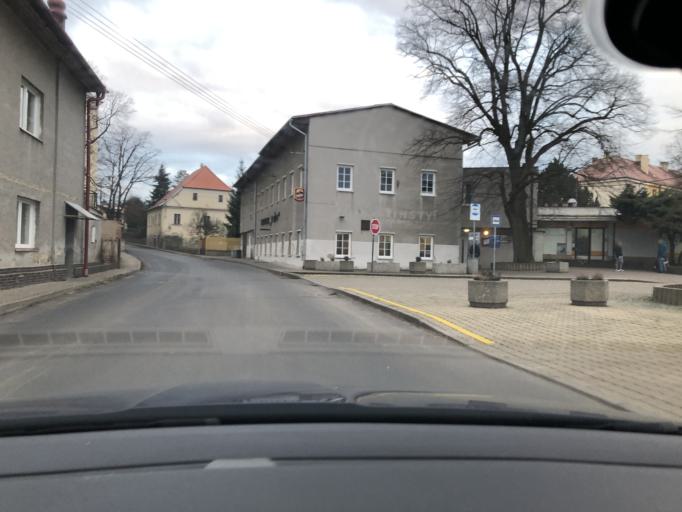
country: CZ
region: Ustecky
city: Rehlovice
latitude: 50.6074
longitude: 13.9523
